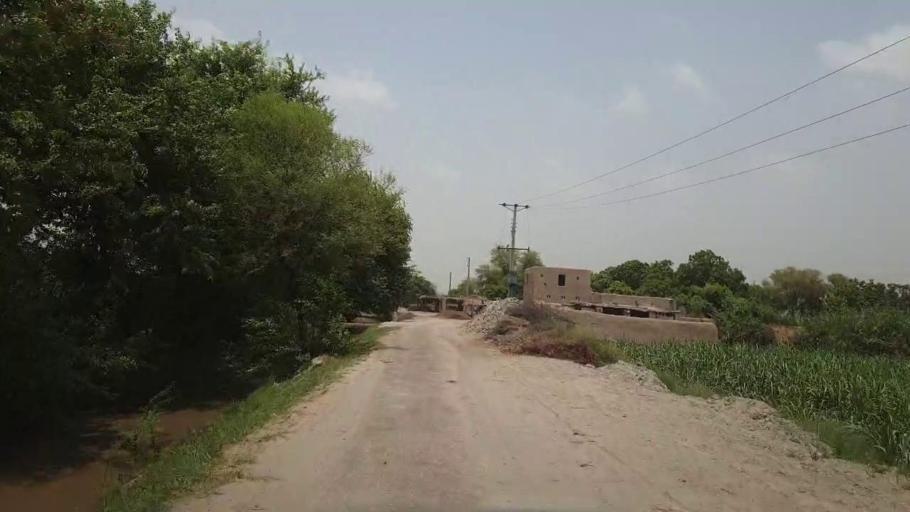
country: PK
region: Sindh
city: Sobhadero
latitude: 27.4357
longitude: 68.4096
